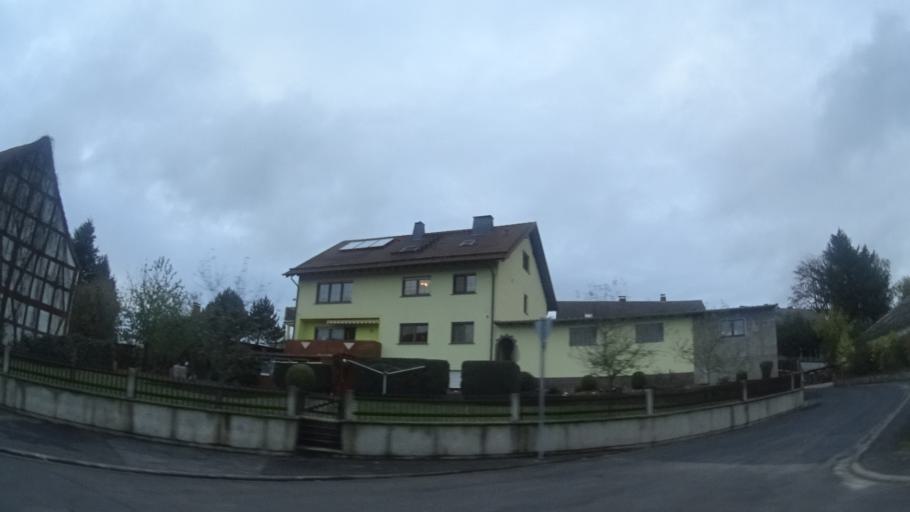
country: DE
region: Hesse
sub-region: Regierungsbezirk Giessen
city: Freiensteinau
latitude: 50.4159
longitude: 9.4198
